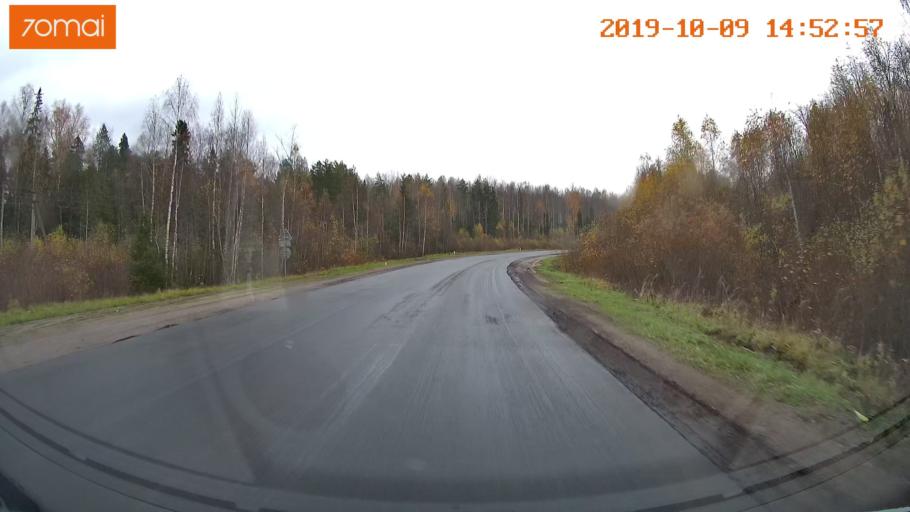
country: RU
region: Kostroma
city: Chistyye Bory
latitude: 58.3733
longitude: 41.6349
